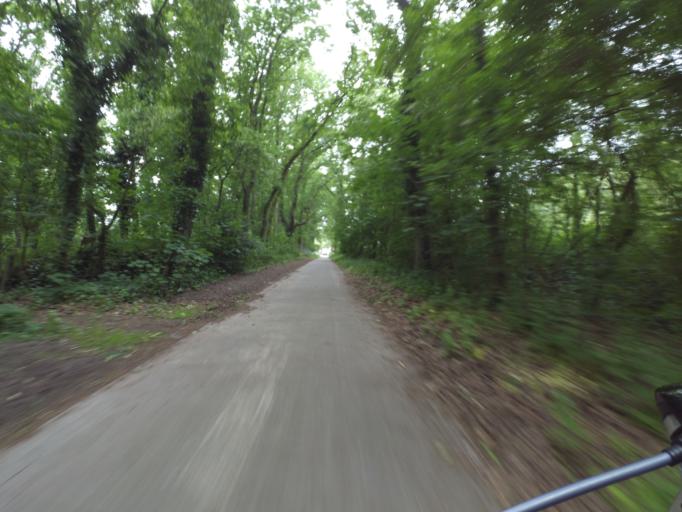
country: NL
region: Gelderland
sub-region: Gemeente Renkum
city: Wolfheze
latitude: 52.0048
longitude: 5.7950
